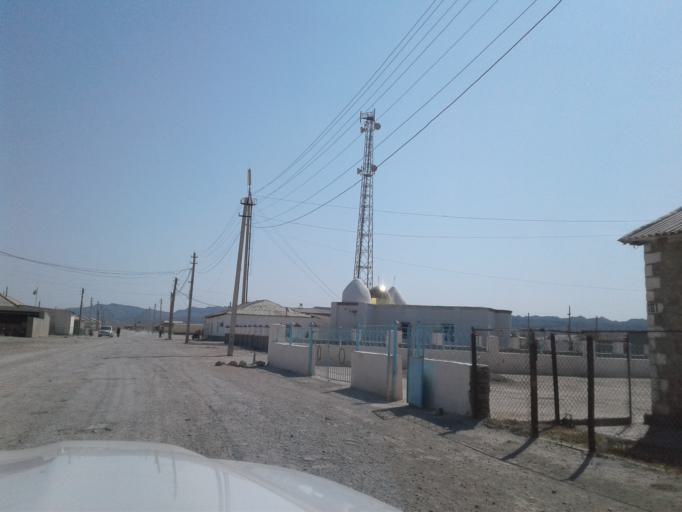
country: TM
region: Balkan
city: Gazanjyk
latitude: 39.1491
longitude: 55.3106
